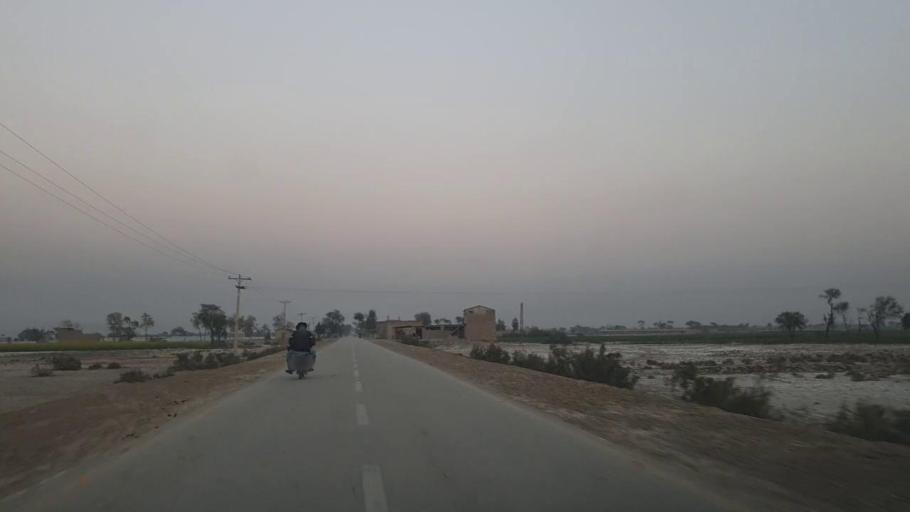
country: PK
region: Sindh
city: Naushahro Firoz
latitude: 26.8488
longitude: 68.0519
